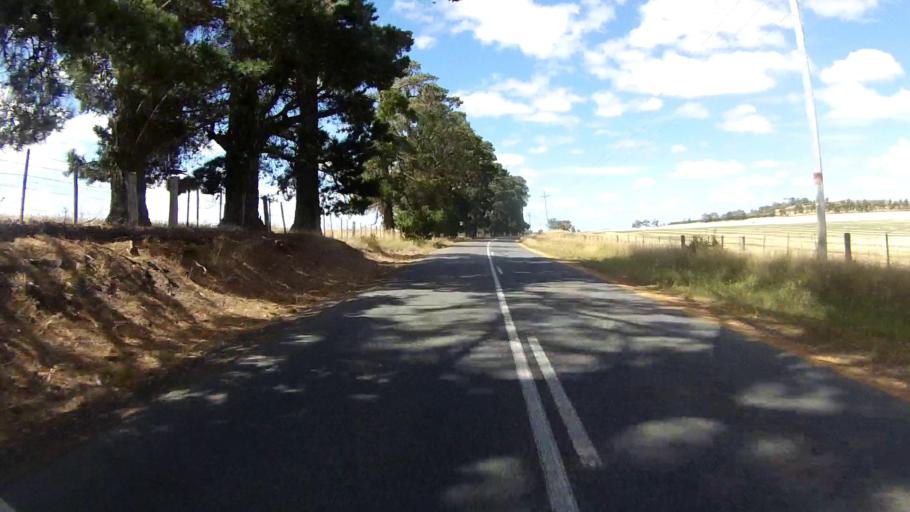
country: AU
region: Tasmania
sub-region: Sorell
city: Sorell
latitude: -42.6384
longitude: 147.4328
